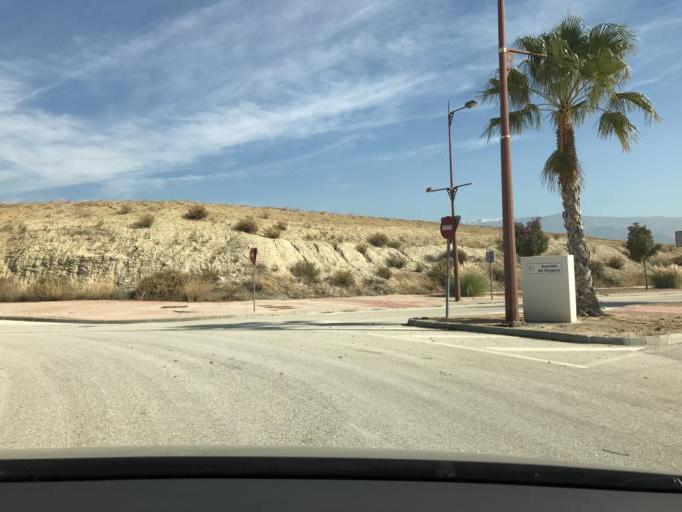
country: ES
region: Andalusia
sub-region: Provincia de Granada
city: Escuzar
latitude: 37.0844
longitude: -3.7483
